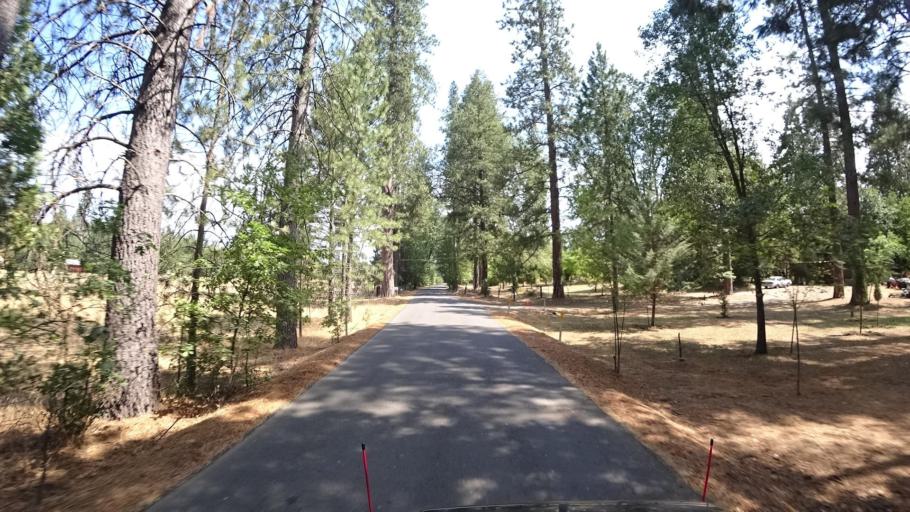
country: US
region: California
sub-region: Mariposa County
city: Midpines
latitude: 37.7139
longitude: -120.0968
